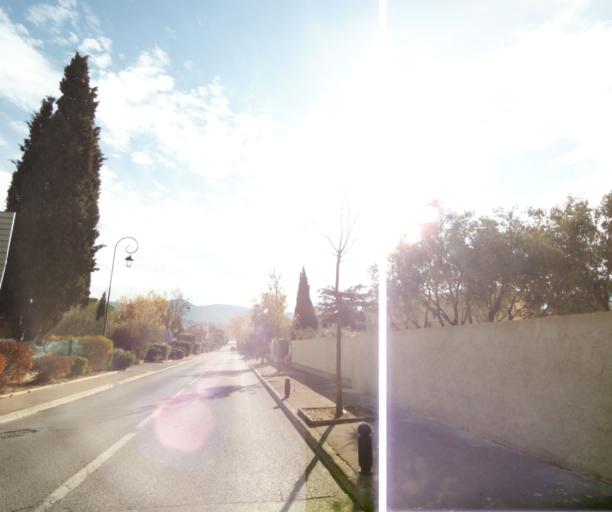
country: FR
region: Provence-Alpes-Cote d'Azur
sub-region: Departement des Bouches-du-Rhone
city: Gemenos
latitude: 43.3005
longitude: 5.6192
